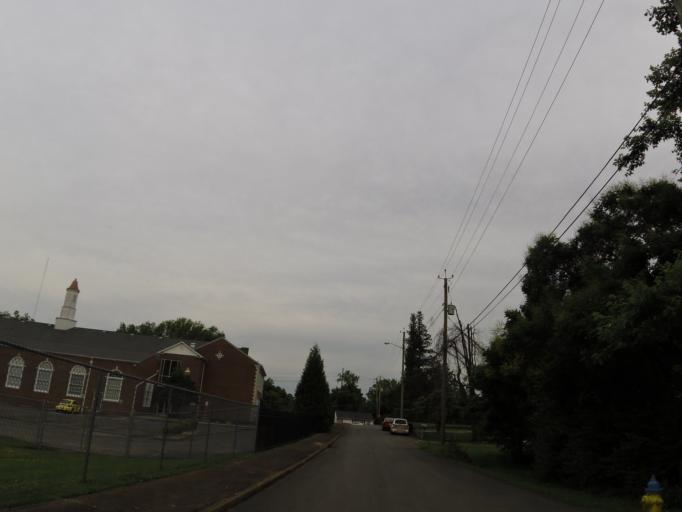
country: US
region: Tennessee
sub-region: Knox County
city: Knoxville
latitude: 35.9574
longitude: -83.9559
